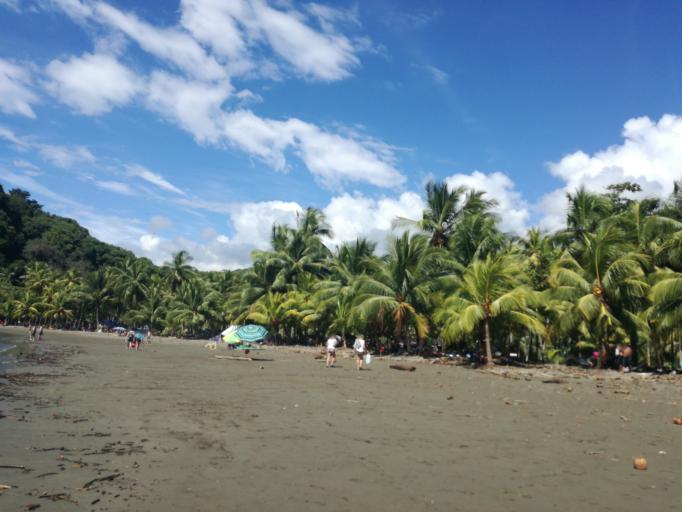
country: CR
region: San Jose
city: Mercedes
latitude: 9.0904
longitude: -83.6770
